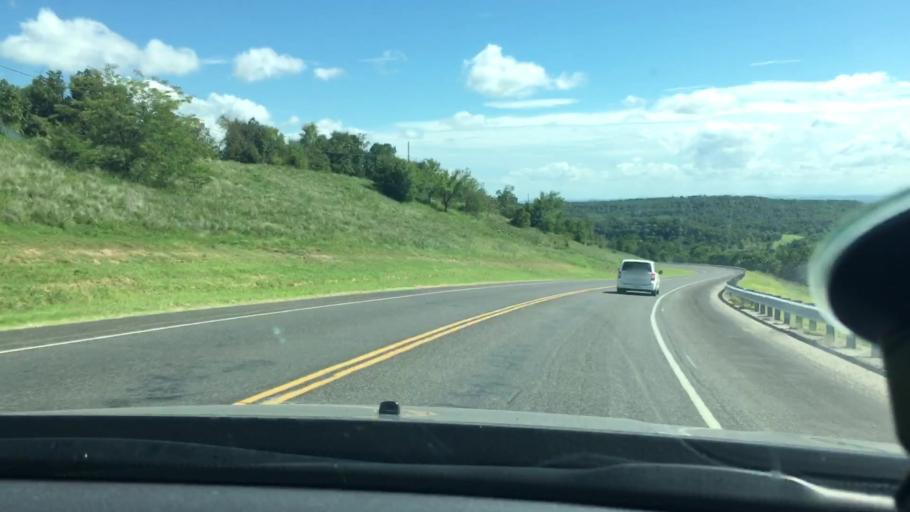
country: US
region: Oklahoma
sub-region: Sequoyah County
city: Vian
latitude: 35.5491
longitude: -94.9699
